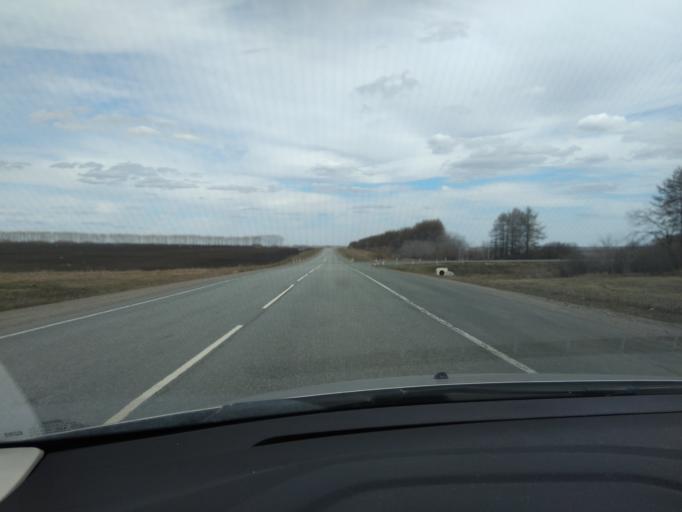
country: RU
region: Sverdlovsk
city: Yelanskiy
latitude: 56.7715
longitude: 62.4455
